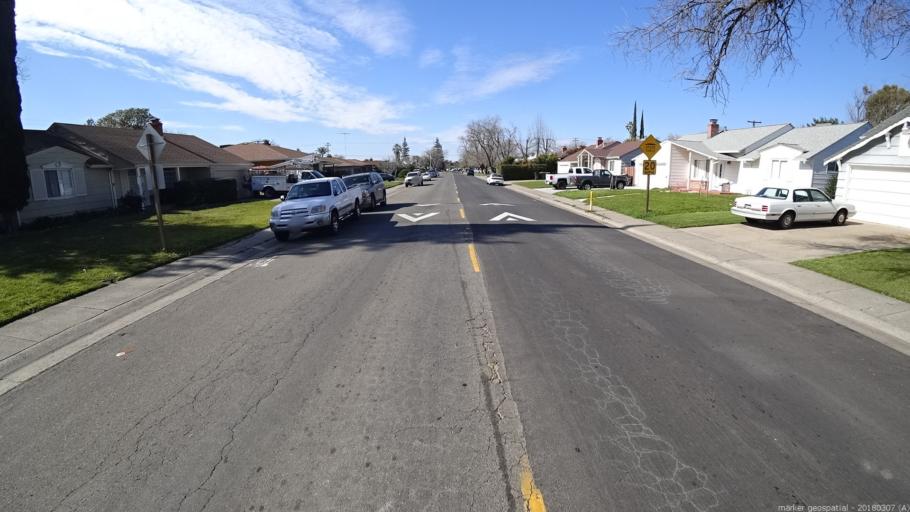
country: US
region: California
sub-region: Sacramento County
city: Parkway
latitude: 38.4911
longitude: -121.4446
